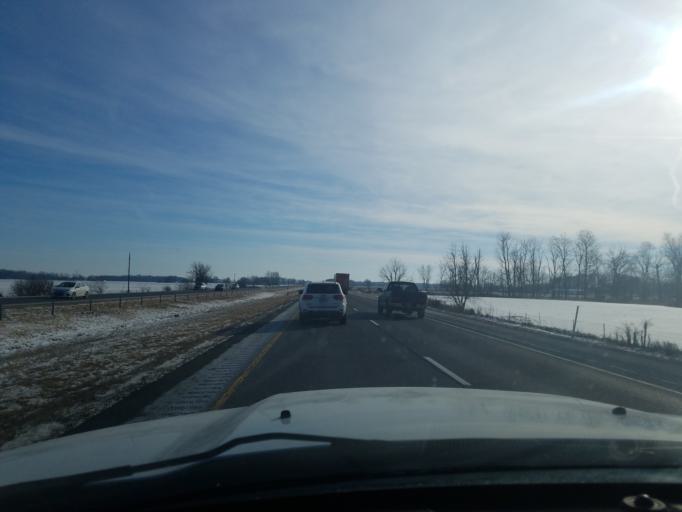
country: US
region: Indiana
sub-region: Madison County
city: Alexandria
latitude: 40.3172
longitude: -85.5590
